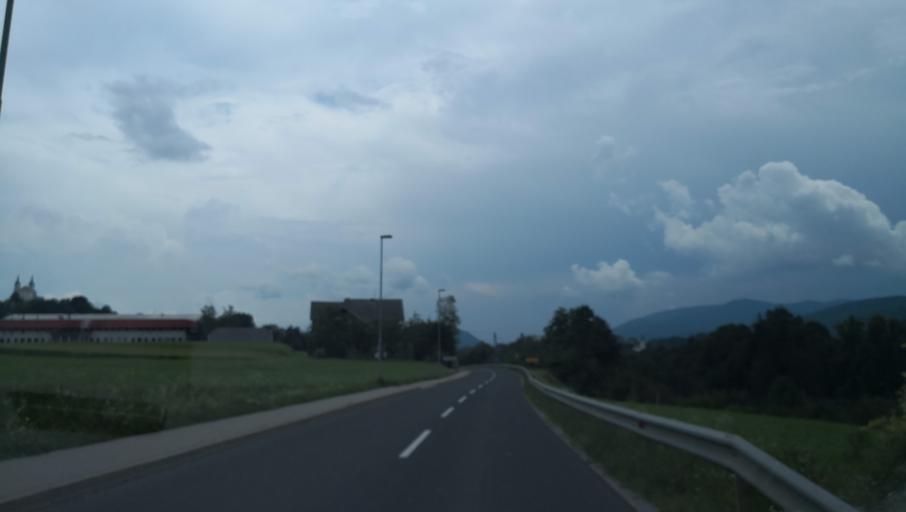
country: SI
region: Zuzemberk
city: Zuzemberk
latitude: 45.8351
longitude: 14.9222
